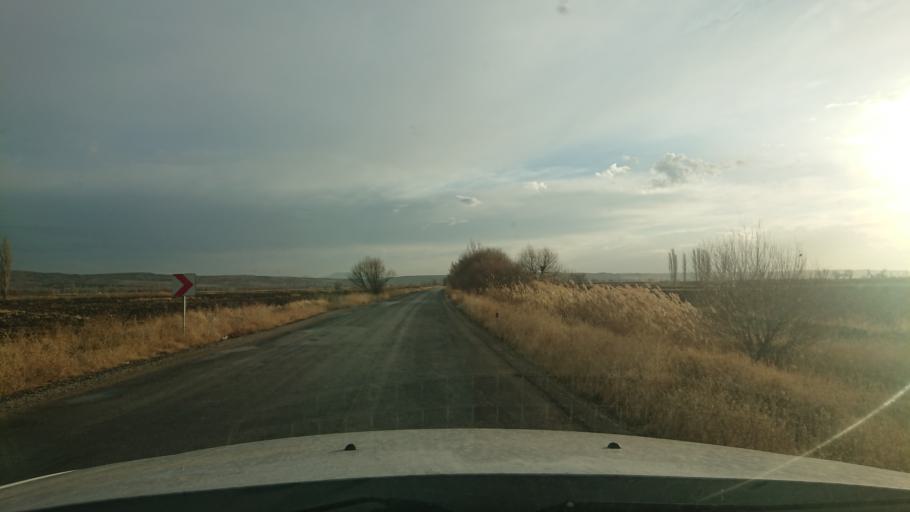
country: TR
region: Aksaray
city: Acipinar
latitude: 38.4758
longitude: 33.8655
